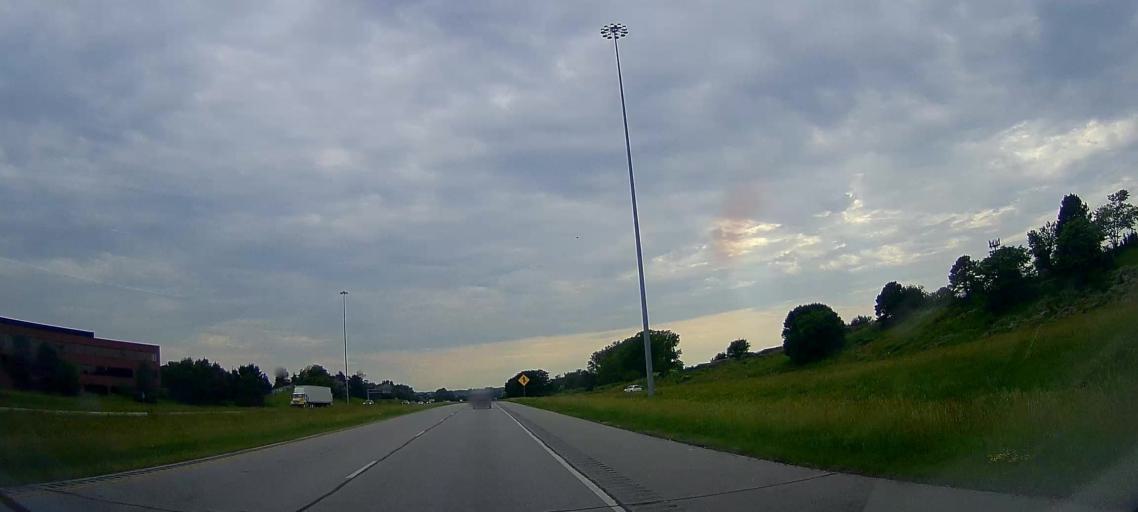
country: US
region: Iowa
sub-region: Pottawattamie County
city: Carter Lake
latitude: 41.3407
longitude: -96.0266
